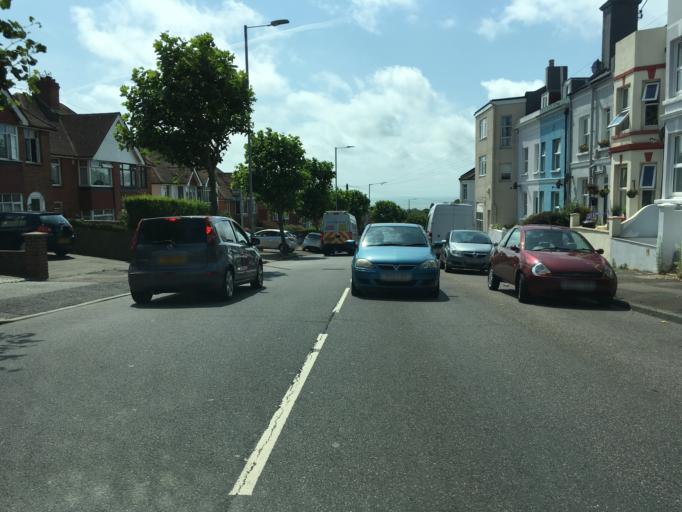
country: GB
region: England
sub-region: East Sussex
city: Hastings
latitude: 50.8676
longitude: 0.6003
